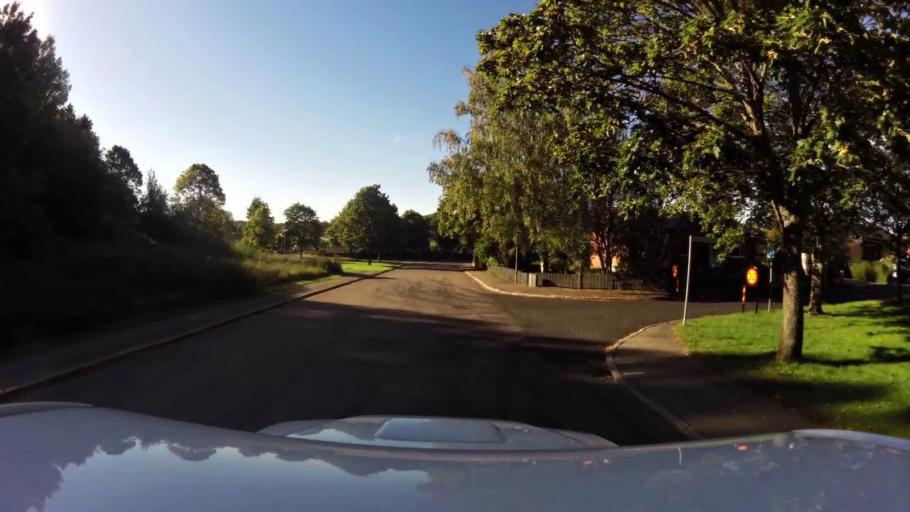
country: SE
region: OEstergoetland
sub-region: Linkopings Kommun
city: Linkoping
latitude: 58.3887
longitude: 15.6438
